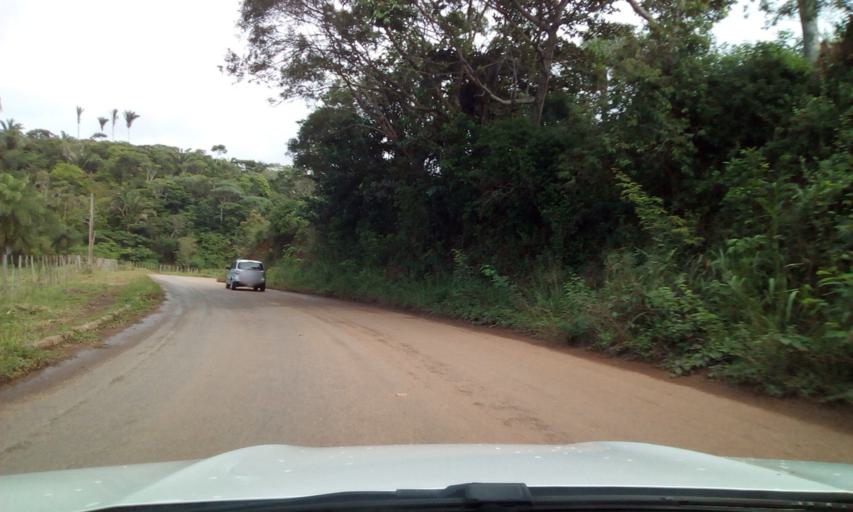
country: BR
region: Paraiba
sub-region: Areia
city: Areia
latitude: -6.9603
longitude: -35.6872
